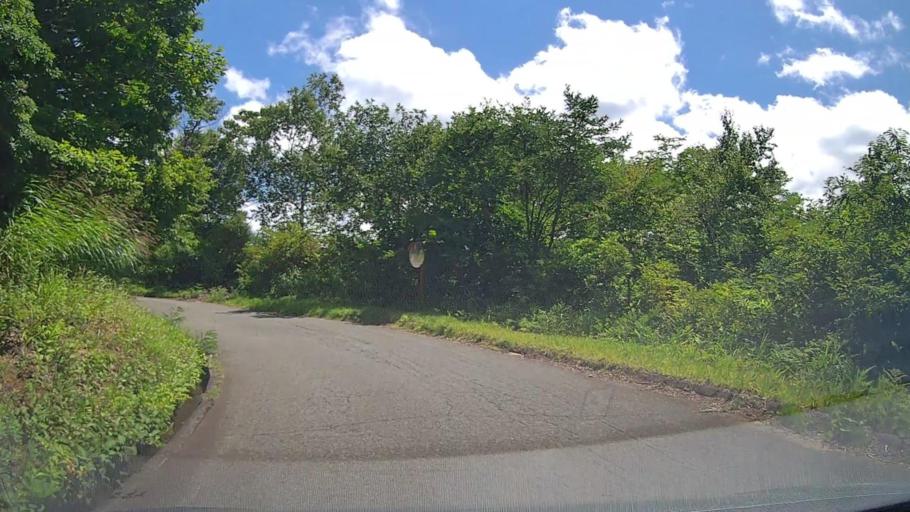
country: JP
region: Nagano
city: Iiyama
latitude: 36.9344
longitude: 138.4539
